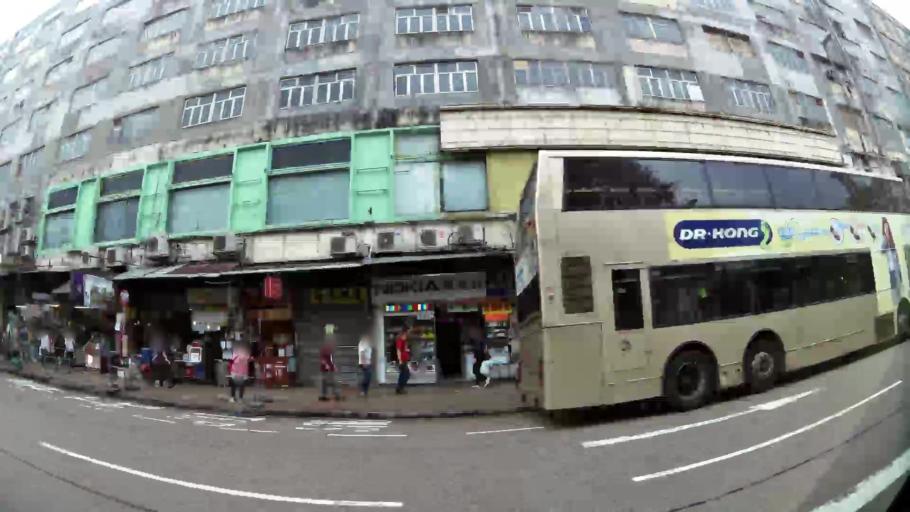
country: HK
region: Kowloon City
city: Kowloon
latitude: 22.3135
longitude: 114.2247
